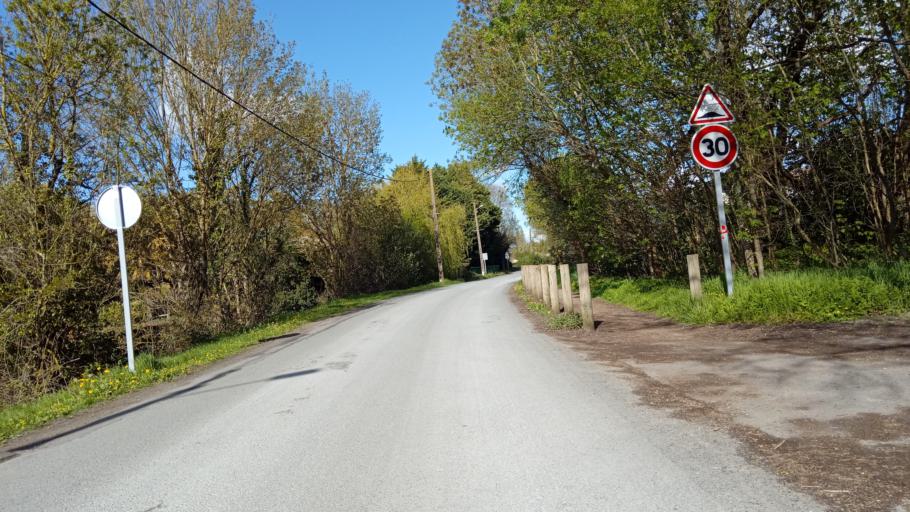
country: FR
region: Poitou-Charentes
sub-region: Departement de la Charente-Maritime
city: Verines
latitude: 46.1468
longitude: -0.9451
